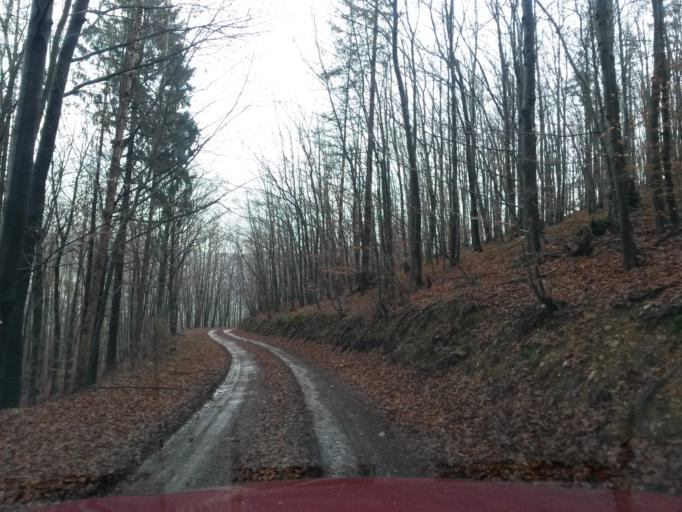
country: SK
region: Kosicky
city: Dobsina
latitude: 48.7446
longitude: 20.4034
